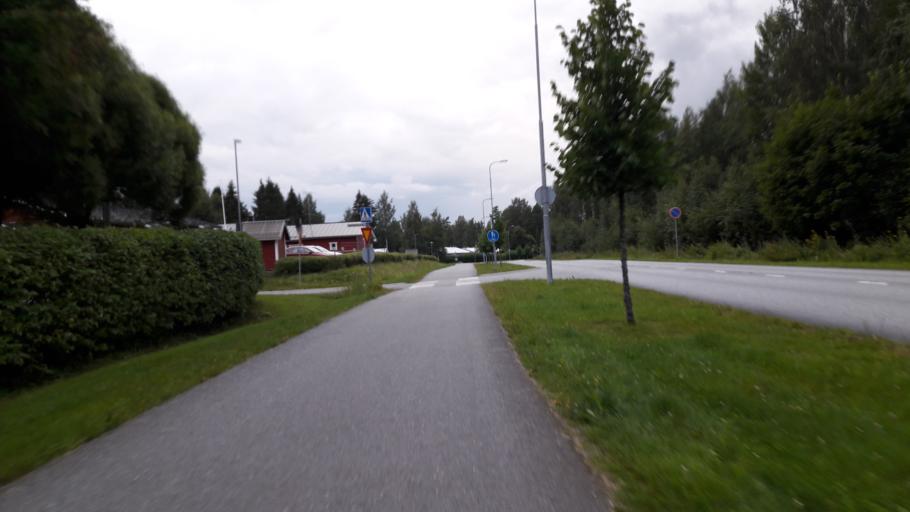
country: FI
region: North Karelia
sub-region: Joensuu
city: Joensuu
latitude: 62.5356
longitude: 29.8373
